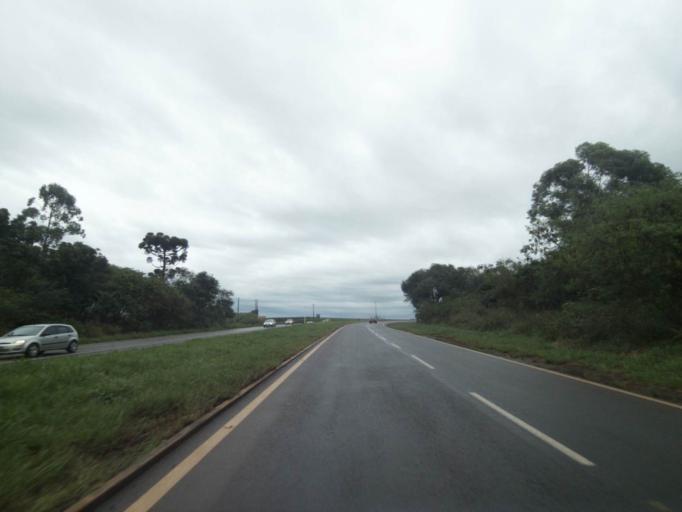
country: BR
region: Parana
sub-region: Toledo
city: Toledo
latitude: -24.6901
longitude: -53.7639
